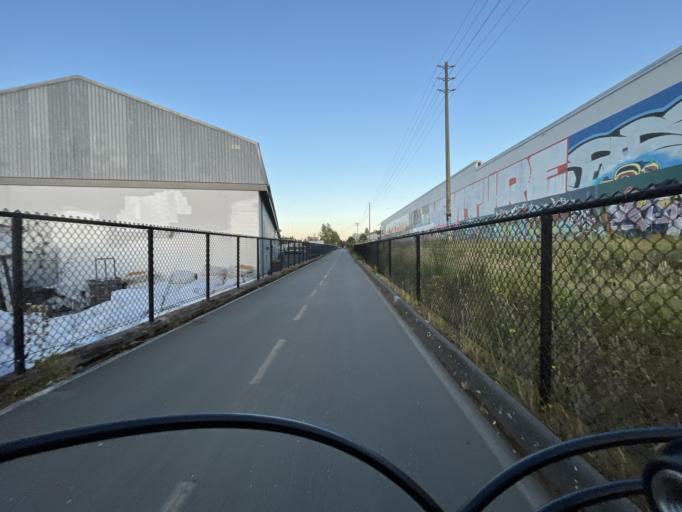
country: CA
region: British Columbia
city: Victoria
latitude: 48.4353
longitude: -123.3972
